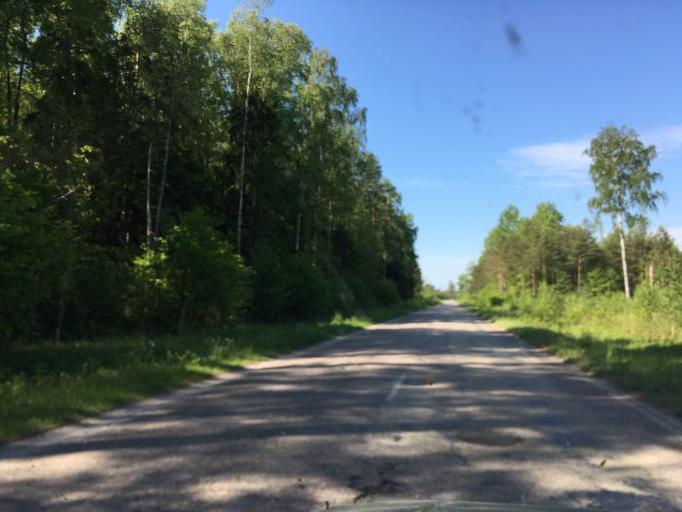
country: LV
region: Ventspils
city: Ventspils
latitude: 57.4861
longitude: 21.7788
